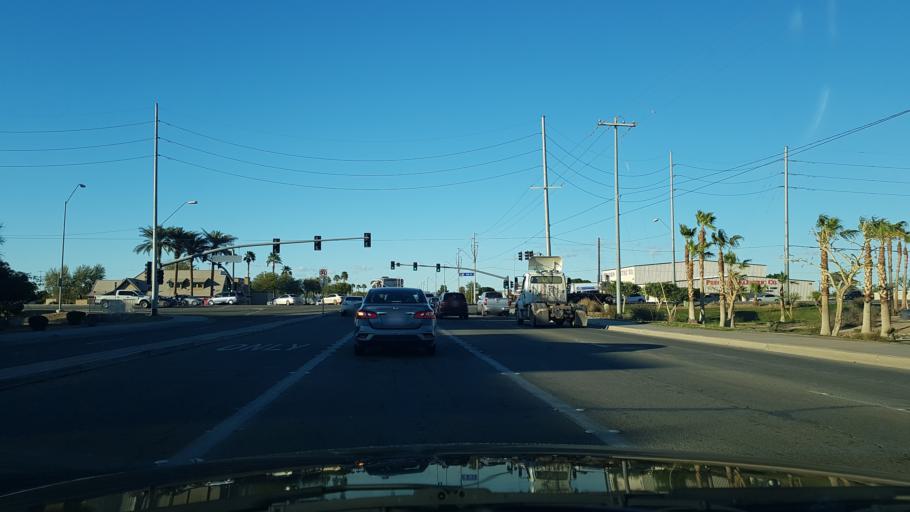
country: US
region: Arizona
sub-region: Yuma County
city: Yuma
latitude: 32.6978
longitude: -114.5988
